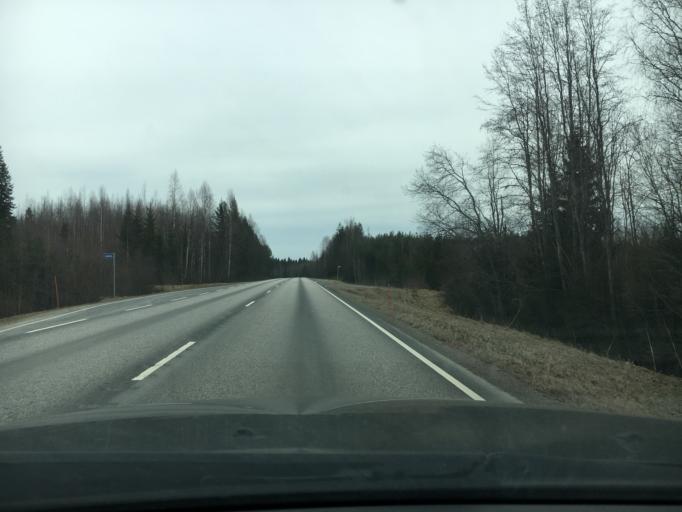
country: FI
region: Central Finland
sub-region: AEaenekoski
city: Sumiainen
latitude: 62.5843
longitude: 26.1512
